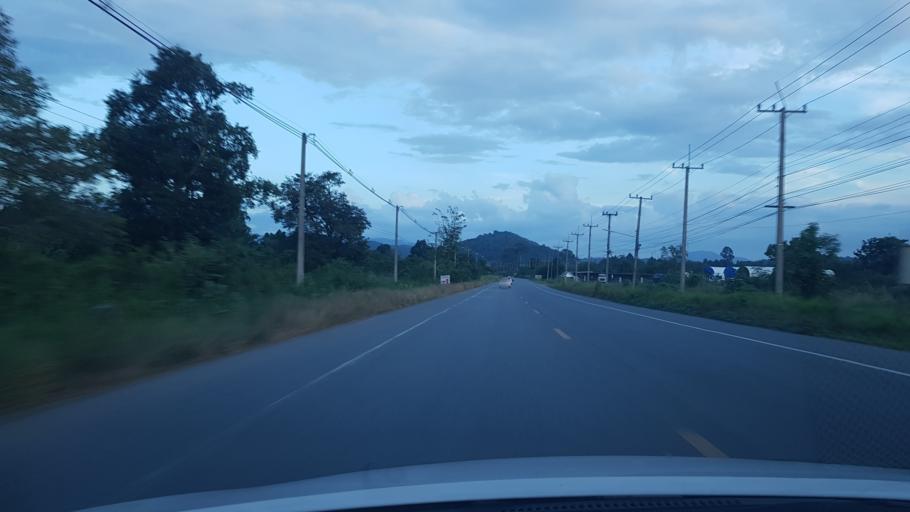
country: TH
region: Sara Buri
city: Kaeng Khoi
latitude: 14.4766
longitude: 101.0586
